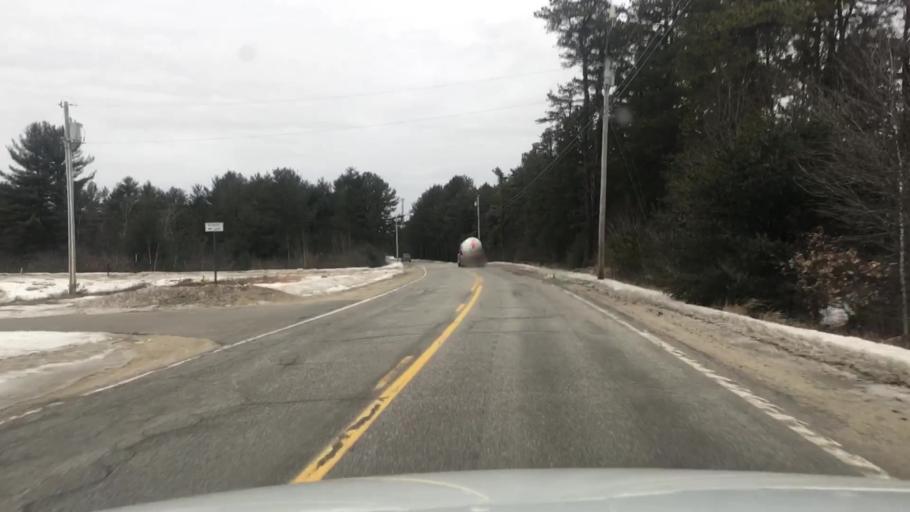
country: US
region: Maine
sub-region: York County
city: Shapleigh
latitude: 43.5673
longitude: -70.8592
